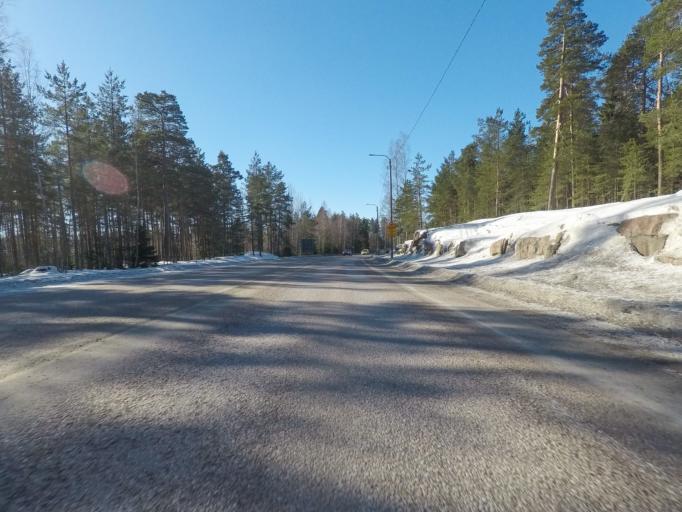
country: FI
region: Uusimaa
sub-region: Helsinki
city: Kirkkonummi
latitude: 60.2717
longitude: 24.4509
